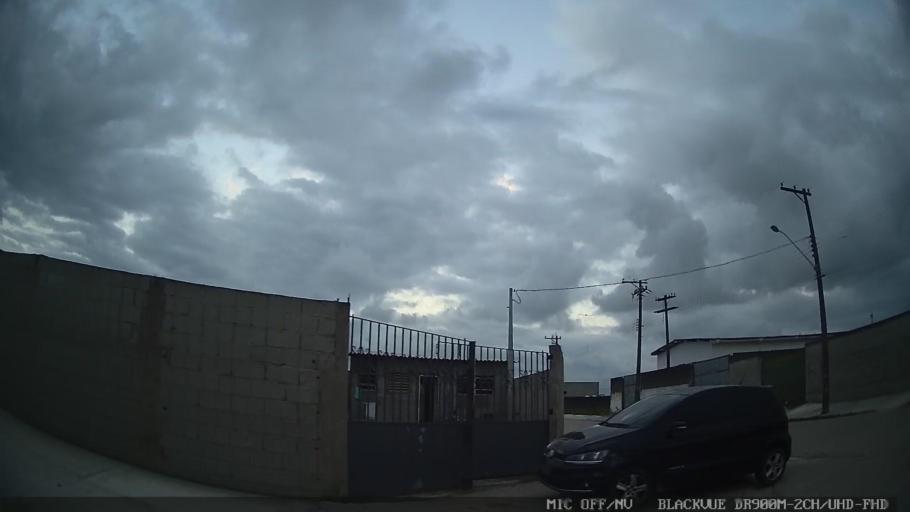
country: BR
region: Sao Paulo
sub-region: Itanhaem
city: Itanhaem
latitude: -24.1890
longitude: -46.8317
